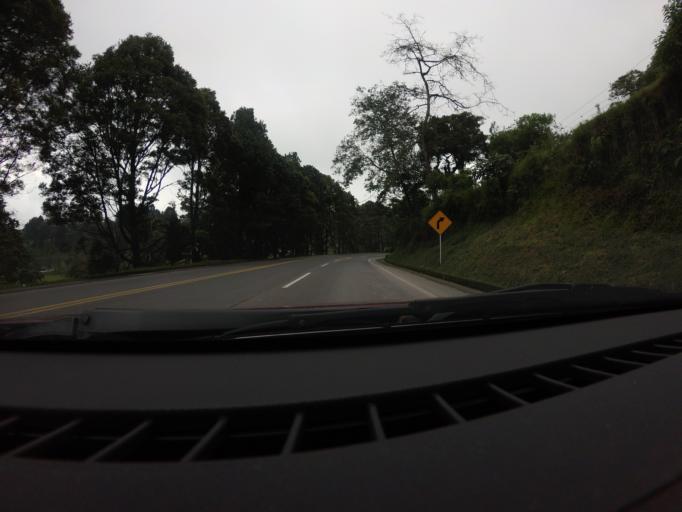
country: CO
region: Cundinamarca
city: San Francisco
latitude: 4.9321
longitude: -74.3010
